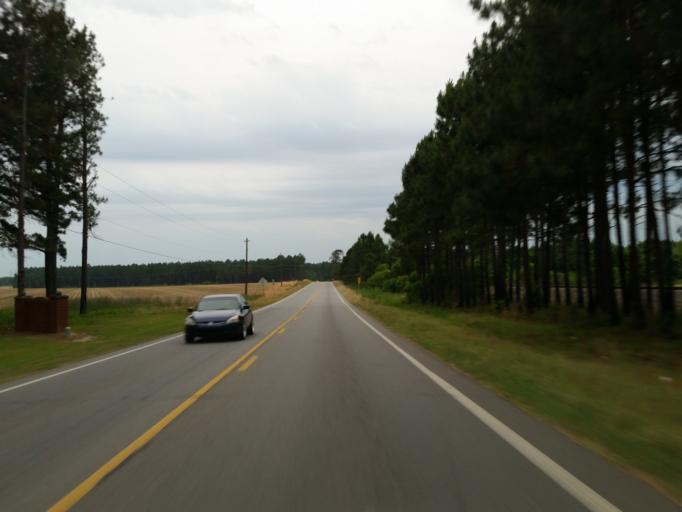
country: US
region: Georgia
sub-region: Dooly County
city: Vienna
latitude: 32.0748
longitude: -83.7958
